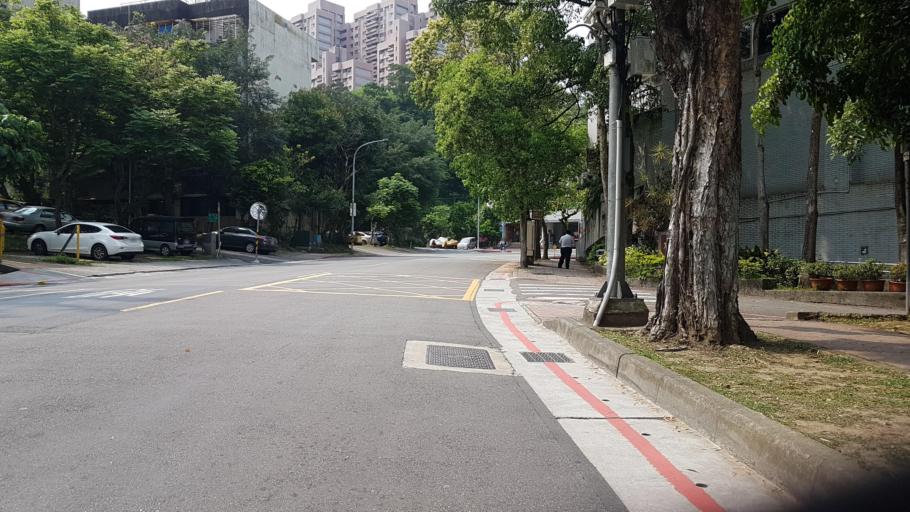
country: TW
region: Taipei
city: Taipei
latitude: 25.0016
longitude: 121.5675
